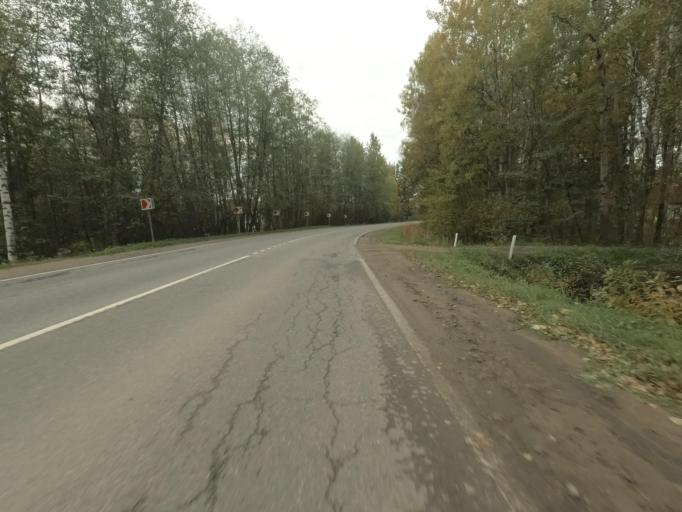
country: RU
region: Leningrad
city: Pavlovo
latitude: 59.7882
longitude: 30.9633
